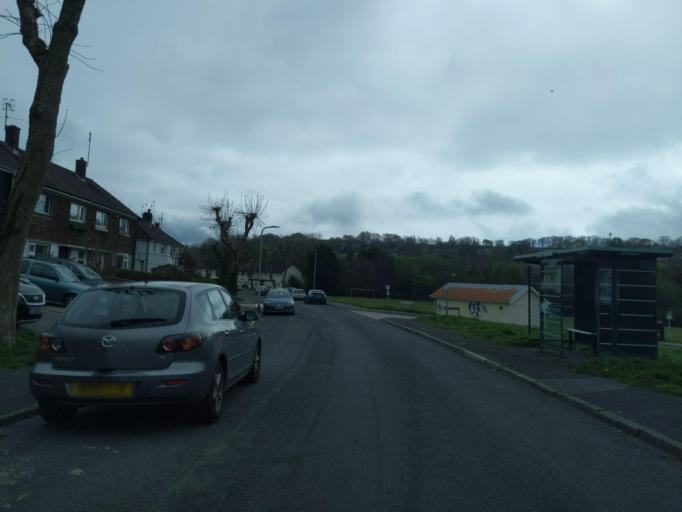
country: GB
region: England
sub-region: Plymouth
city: Plymouth
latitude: 50.4043
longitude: -4.1510
